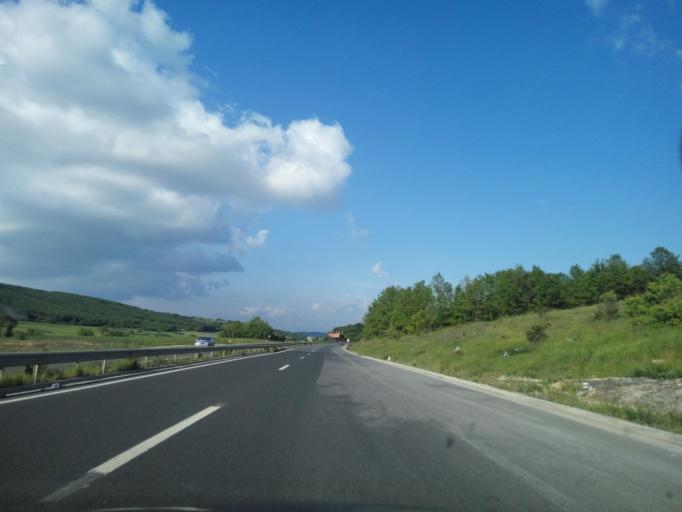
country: XK
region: Prizren
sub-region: Komuna e Malisheves
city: Llazice
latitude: 42.5669
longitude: 20.8341
